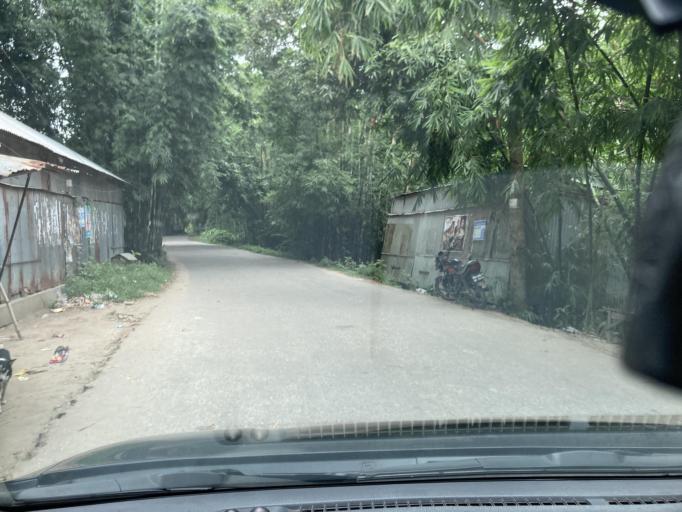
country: BD
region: Dhaka
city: Dohar
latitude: 23.7998
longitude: 90.0470
